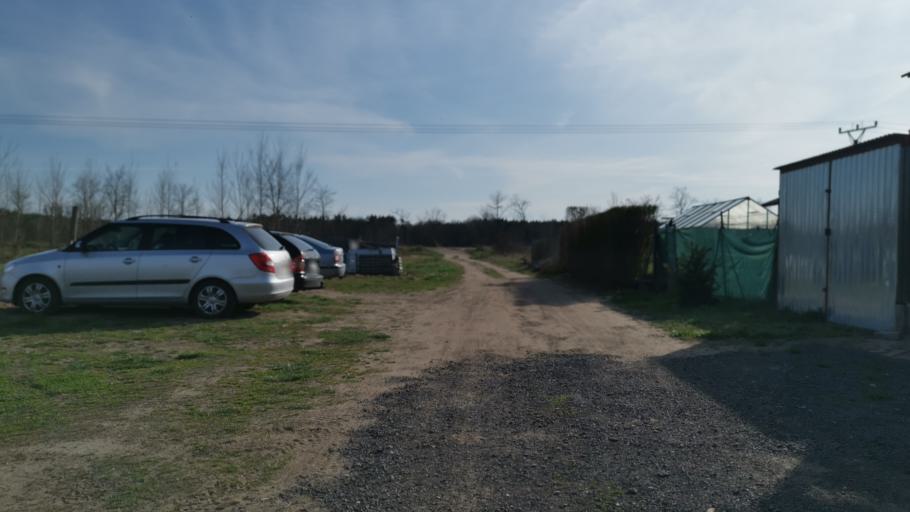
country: CZ
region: South Moravian
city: Tvrdonice
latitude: 48.7263
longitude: 17.0382
